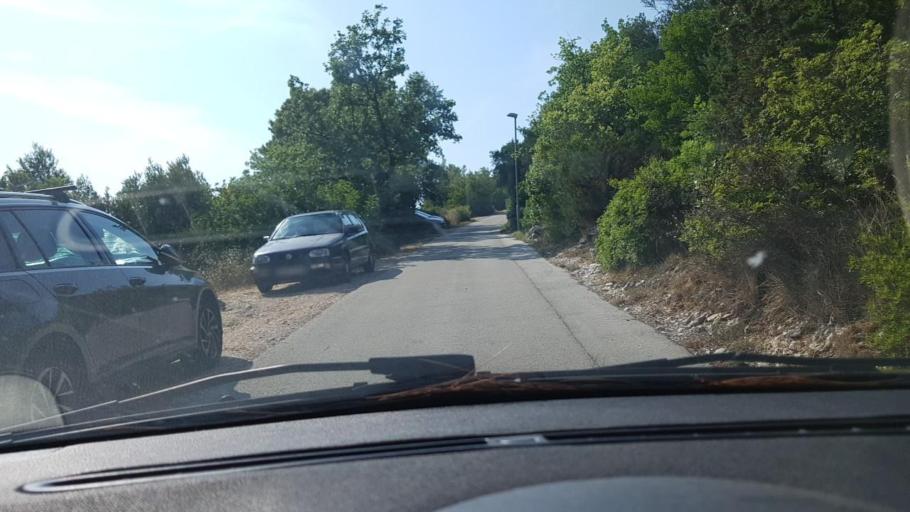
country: HR
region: Dubrovacko-Neretvanska
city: Podgora
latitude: 42.7849
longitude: 17.8589
